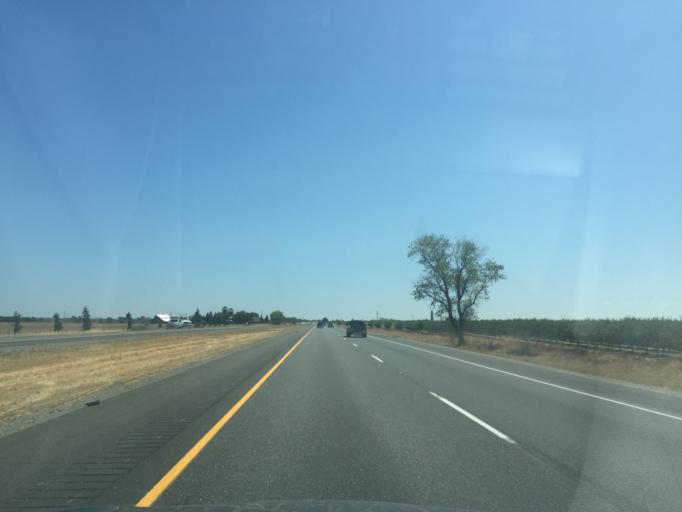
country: US
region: California
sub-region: Tehama County
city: Corning
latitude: 39.9863
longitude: -122.2037
